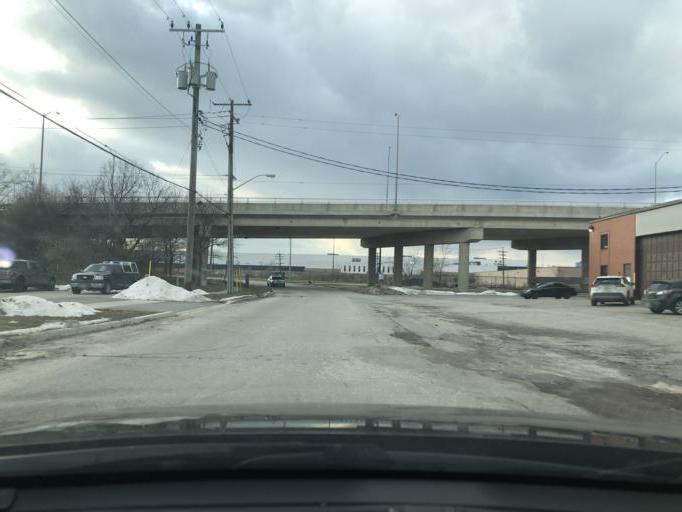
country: CA
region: Ontario
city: Scarborough
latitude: 43.7706
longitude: -79.2925
